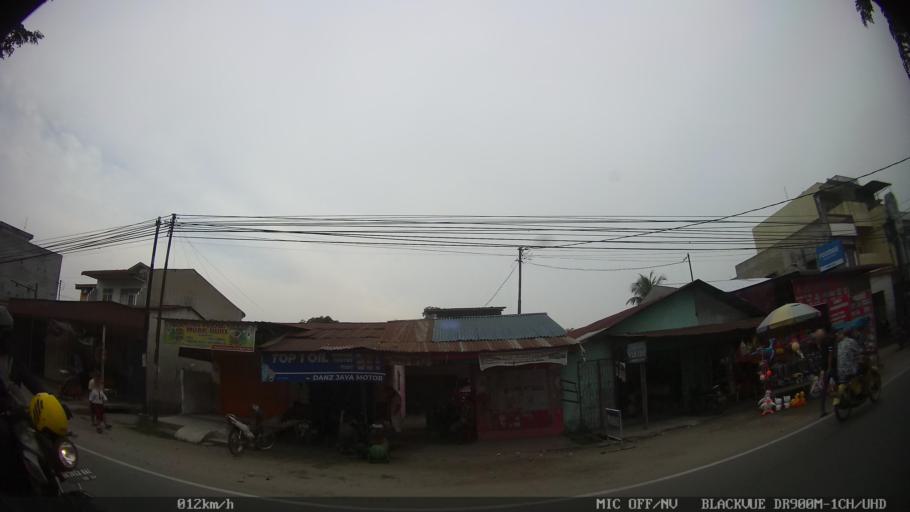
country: ID
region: North Sumatra
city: Deli Tua
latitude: 3.5504
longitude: 98.7163
